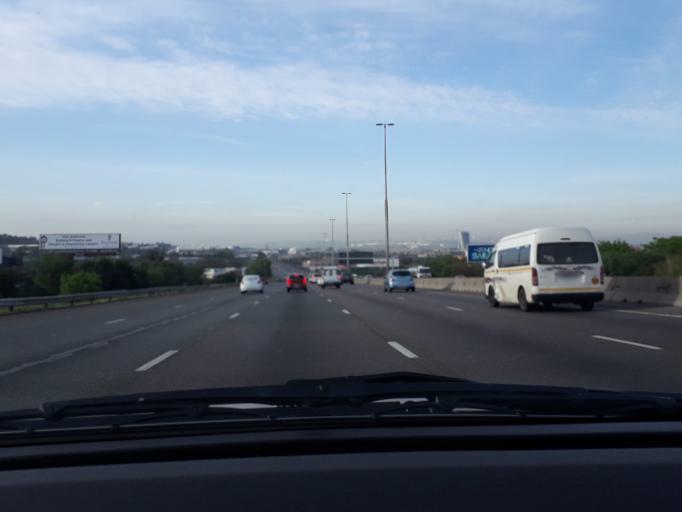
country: ZA
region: Gauteng
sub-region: City of Johannesburg Metropolitan Municipality
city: Midrand
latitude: -25.9881
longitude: 28.1239
